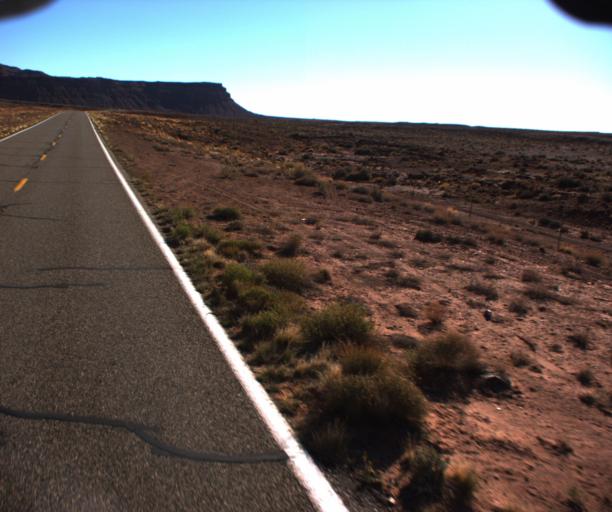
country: US
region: Arizona
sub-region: Coconino County
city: LeChee
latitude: 36.7361
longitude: -111.6387
